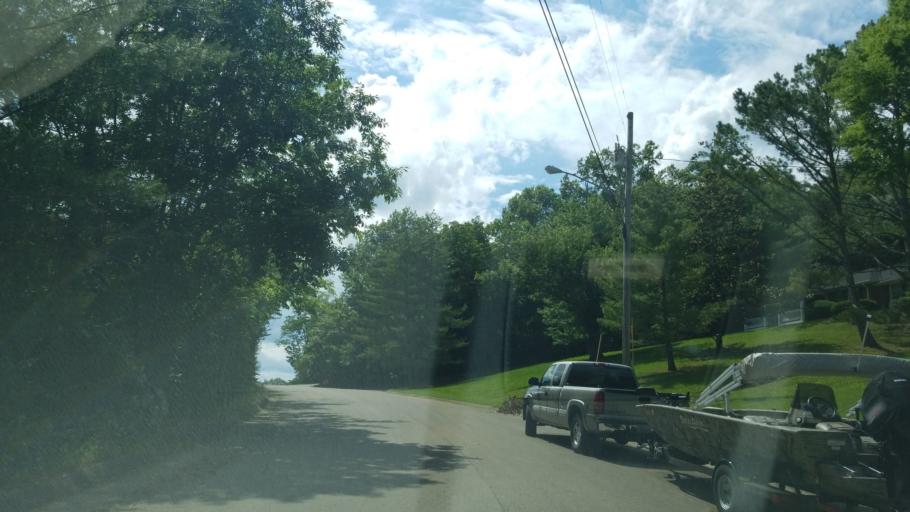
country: US
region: Tennessee
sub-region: Davidson County
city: Forest Hills
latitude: 36.0305
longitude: -86.8517
